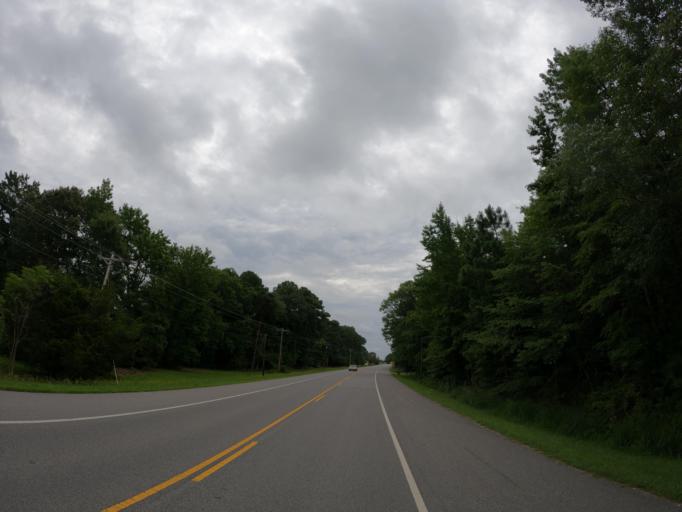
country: US
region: Maryland
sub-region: Saint Mary's County
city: Lexington Park
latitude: 38.1506
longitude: -76.5139
